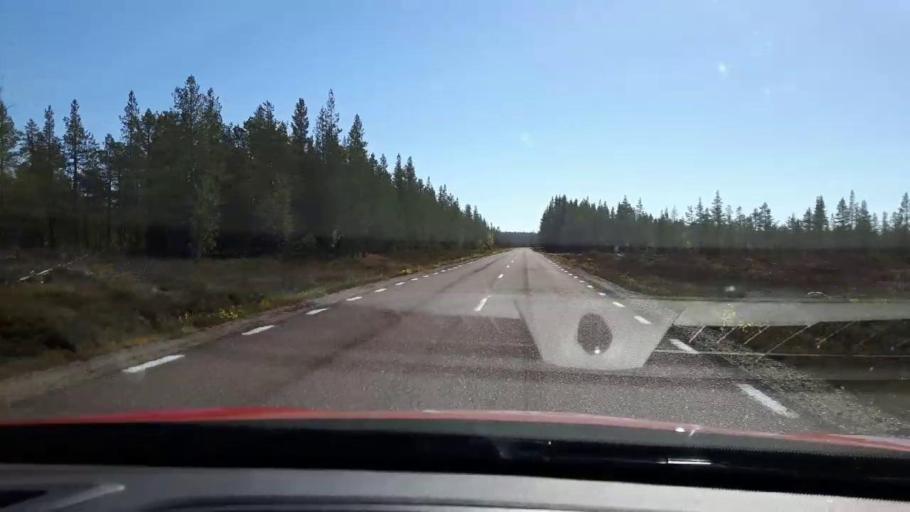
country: SE
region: Jaemtland
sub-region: Harjedalens Kommun
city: Sveg
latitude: 61.7437
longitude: 14.1592
